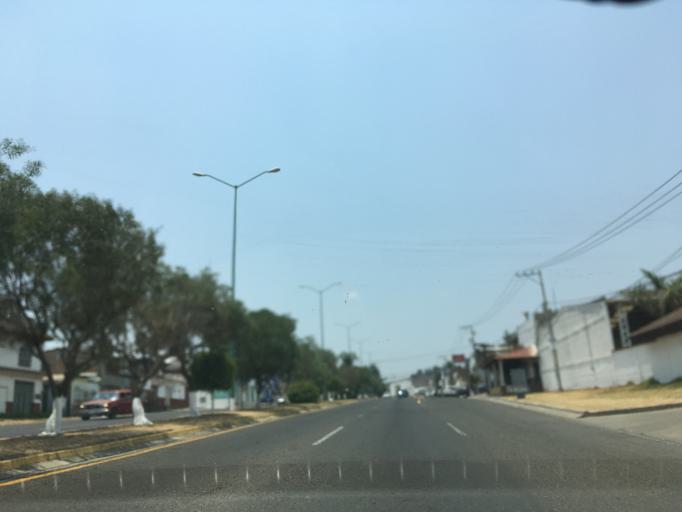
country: MX
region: Michoacan
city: Patzcuaro
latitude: 19.5235
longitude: -101.6154
